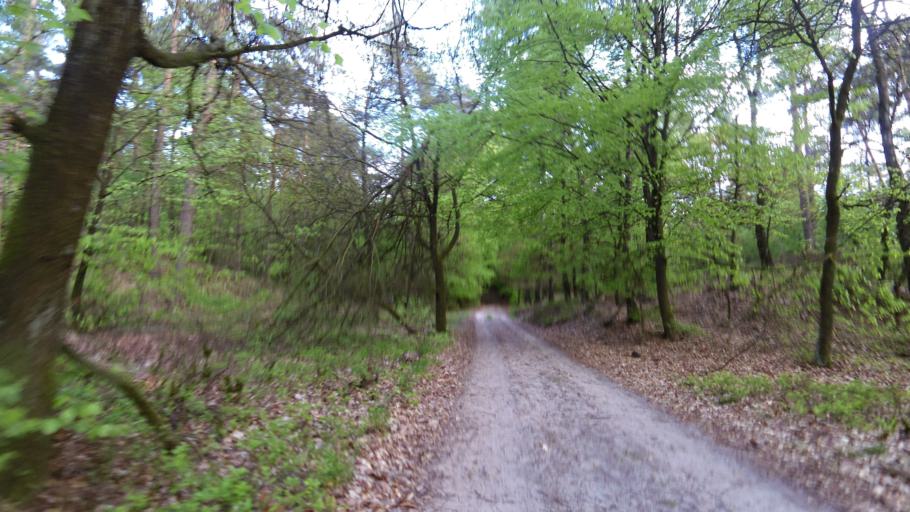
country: NL
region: Gelderland
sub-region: Gemeente Rozendaal
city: Rozendaal
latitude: 52.0237
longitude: 5.9593
